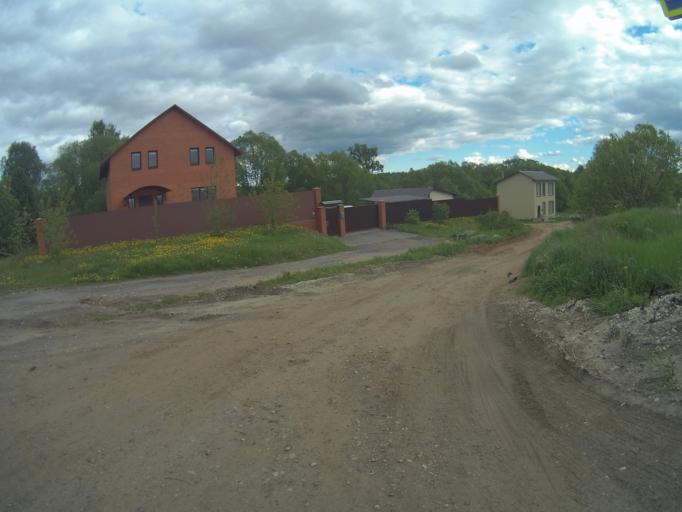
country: RU
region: Vladimir
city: Kommunar
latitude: 56.0666
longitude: 40.4886
